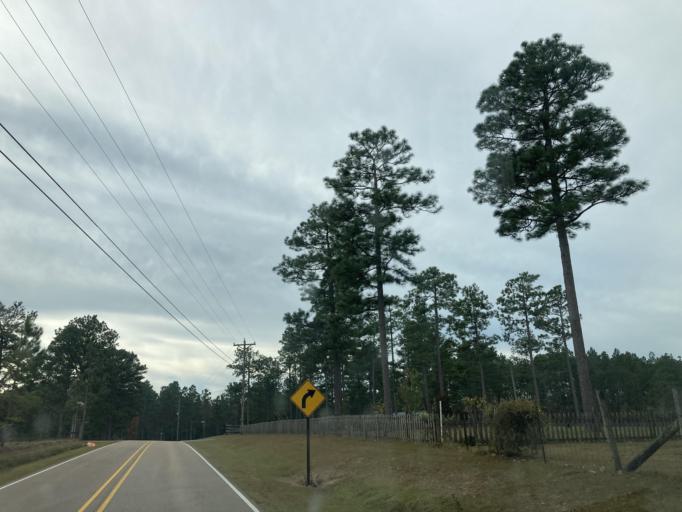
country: US
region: Mississippi
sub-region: Lamar County
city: Purvis
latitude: 31.0996
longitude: -89.4717
